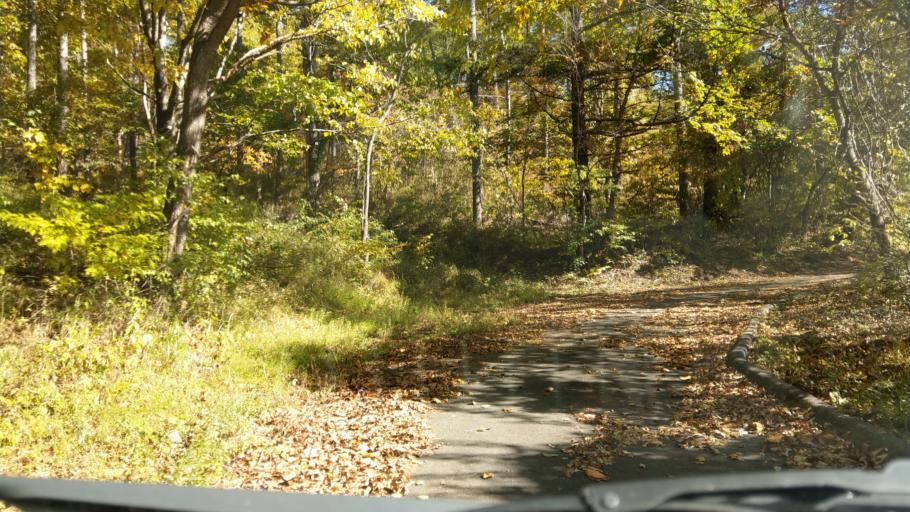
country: JP
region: Nagano
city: Komoro
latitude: 36.3809
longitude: 138.4301
